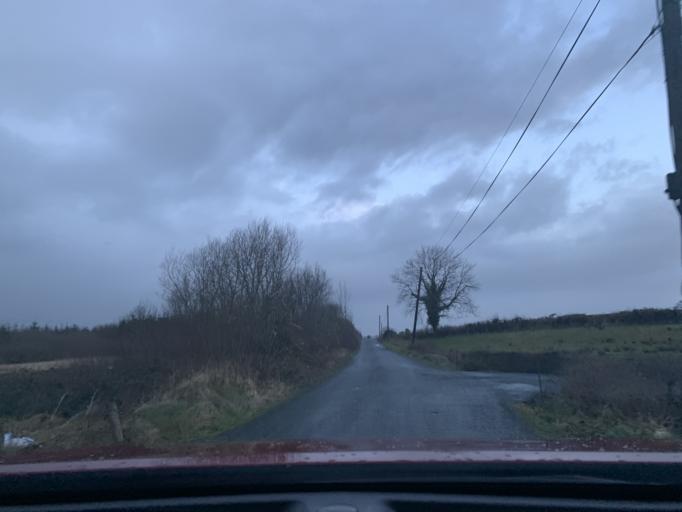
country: IE
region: Connaught
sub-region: Roscommon
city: Ballaghaderreen
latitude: 53.9809
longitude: -8.5441
